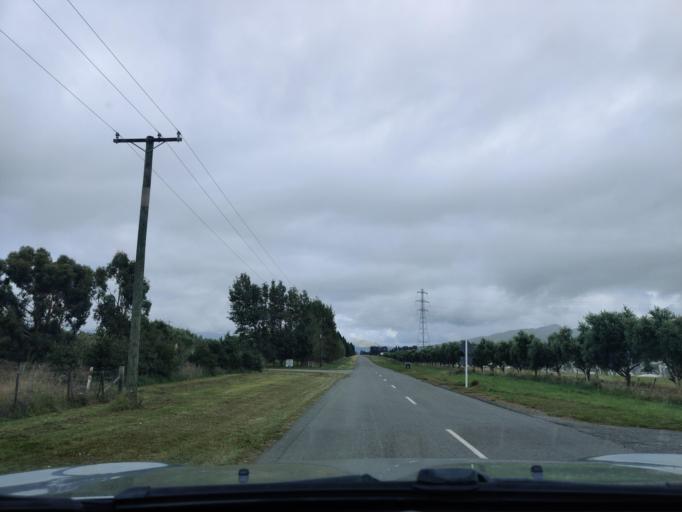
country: NZ
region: Canterbury
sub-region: Hurunui District
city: Amberley
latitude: -43.0764
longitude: 172.7083
